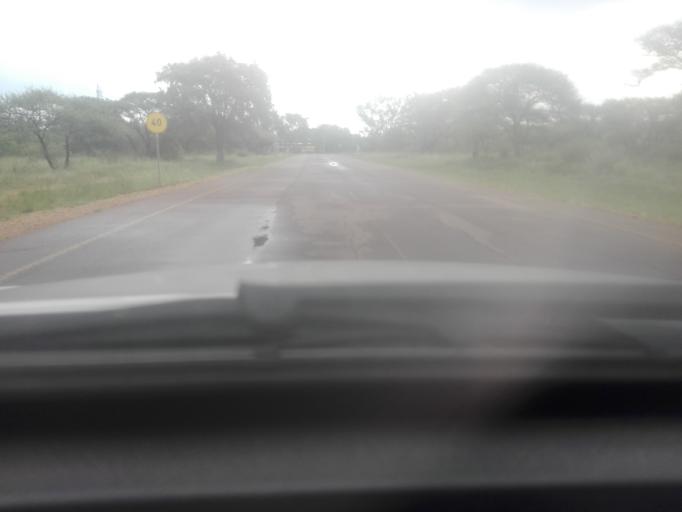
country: BW
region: Kweneng
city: Mmopone
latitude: -24.5602
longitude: 25.9274
